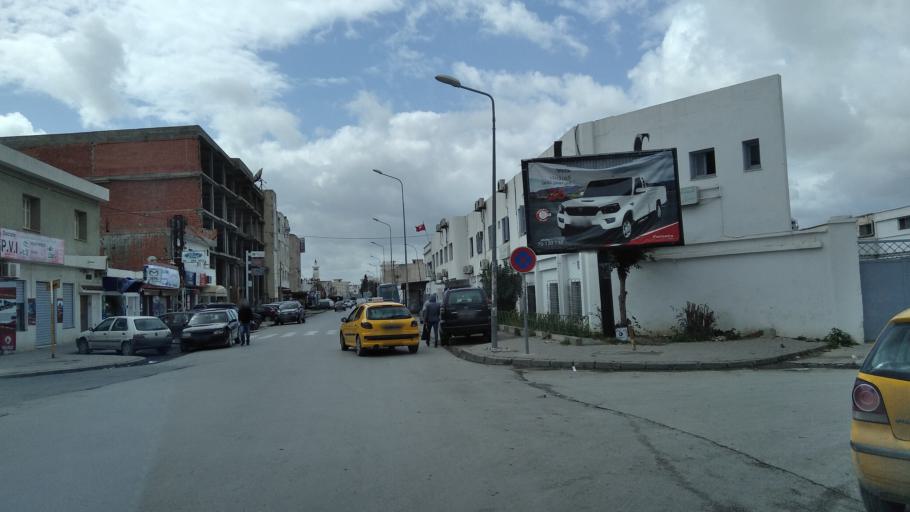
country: TN
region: Bin 'Arus
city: Ben Arous
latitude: 36.7612
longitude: 10.2244
